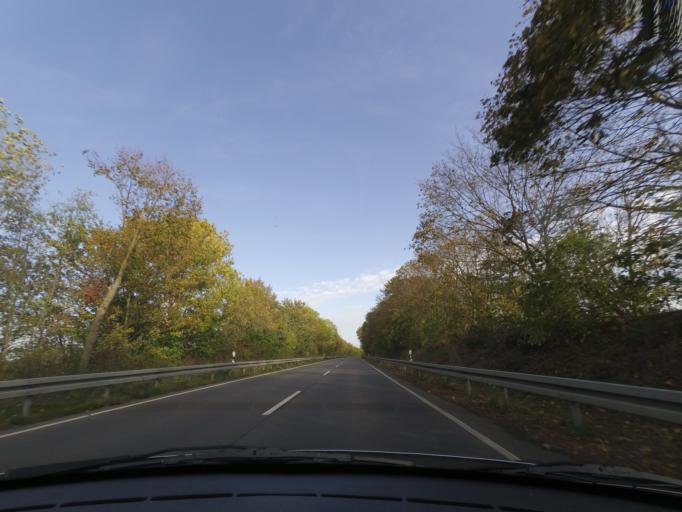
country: DE
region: North Rhine-Westphalia
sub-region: Regierungsbezirk Dusseldorf
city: Neubrueck
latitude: 51.1704
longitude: 6.6090
